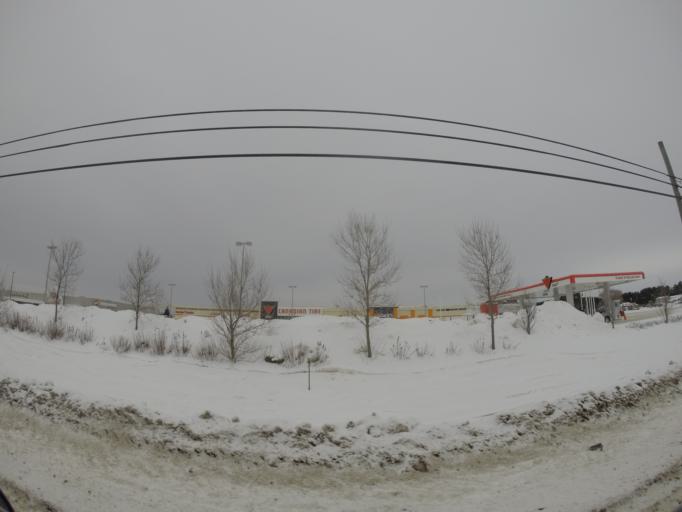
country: CA
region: Ontario
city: Greater Sudbury
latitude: 46.6529
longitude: -80.9846
